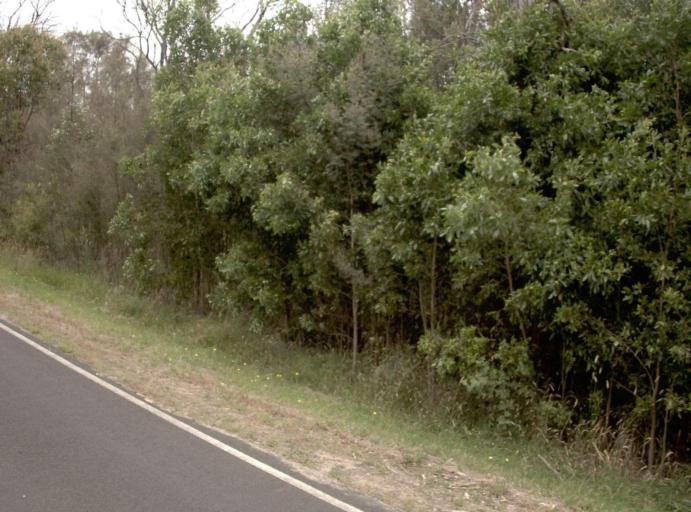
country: AU
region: Victoria
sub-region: Latrobe
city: Traralgon
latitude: -38.4819
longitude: 146.8209
